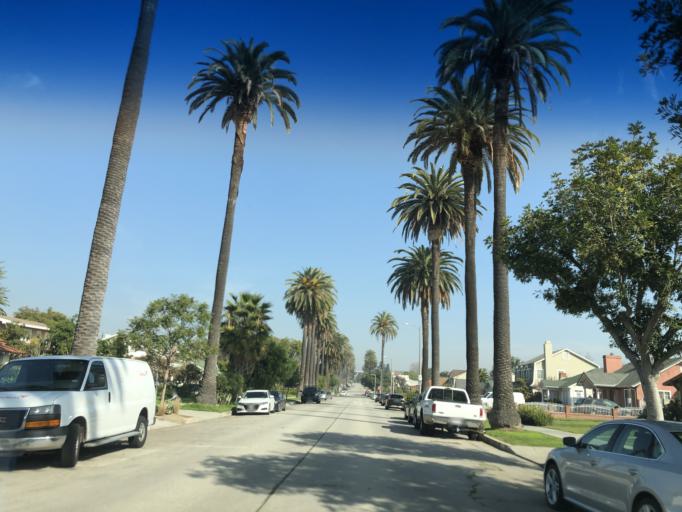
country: US
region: California
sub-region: Los Angeles County
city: Hollywood
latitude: 34.0525
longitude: -118.3271
